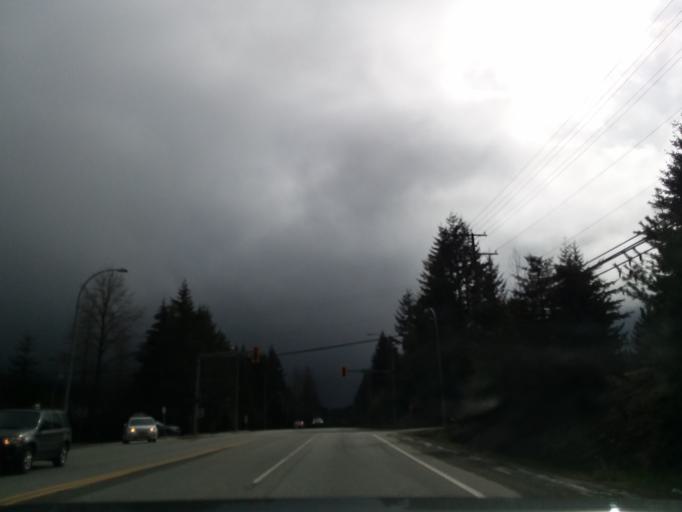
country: CA
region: British Columbia
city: Whistler
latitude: 50.1267
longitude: -122.9558
